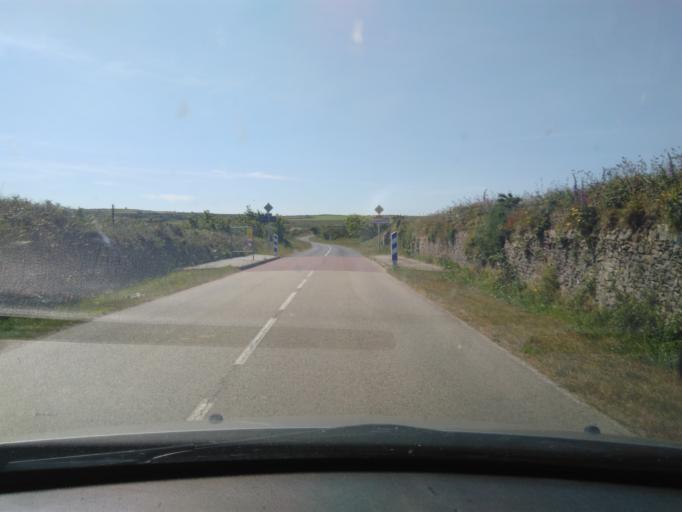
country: FR
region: Lower Normandy
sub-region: Departement de la Manche
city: Beaumont-Hague
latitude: 49.7071
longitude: -1.9315
